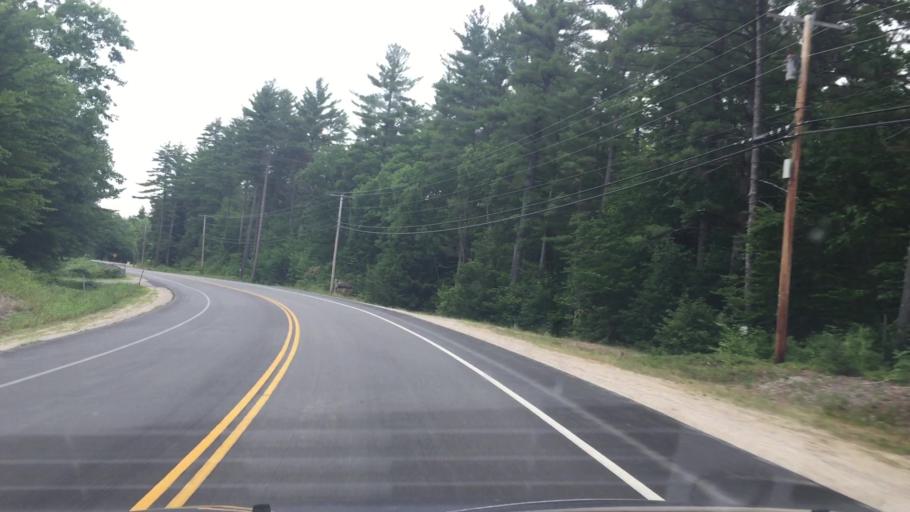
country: US
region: New Hampshire
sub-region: Carroll County
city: Tamworth
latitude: 43.8414
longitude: -71.2646
